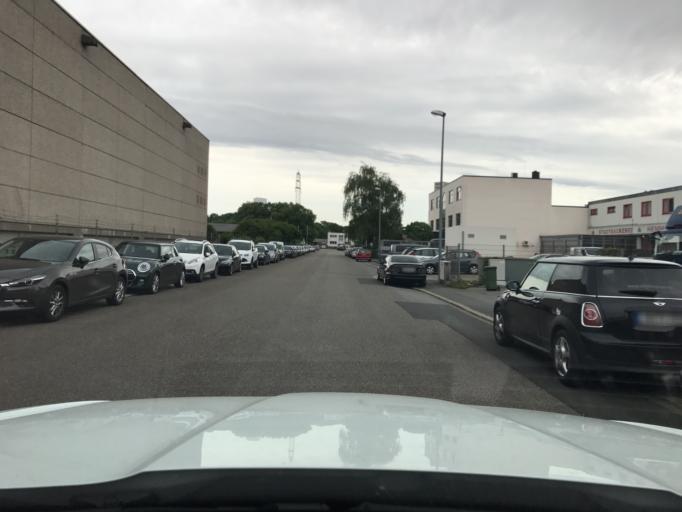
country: DE
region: North Rhine-Westphalia
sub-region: Regierungsbezirk Dusseldorf
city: Muelheim (Ruhr)
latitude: 51.4329
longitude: 6.8575
